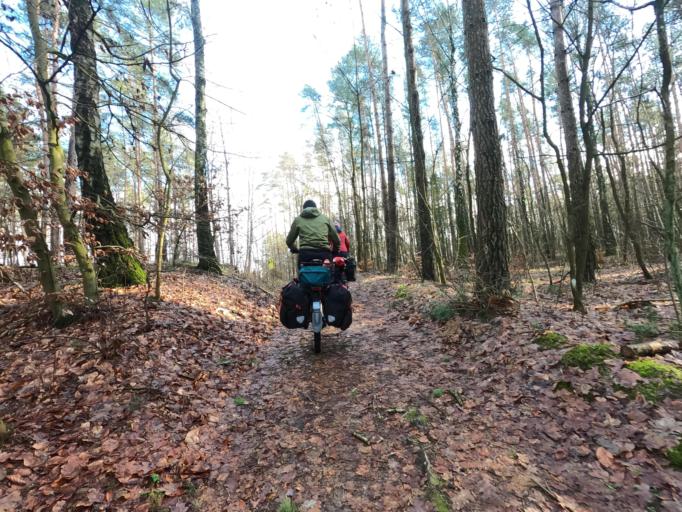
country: PL
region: Greater Poland Voivodeship
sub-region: Powiat pilski
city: Miasteczko Krajenskie
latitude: 53.1011
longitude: 17.0334
